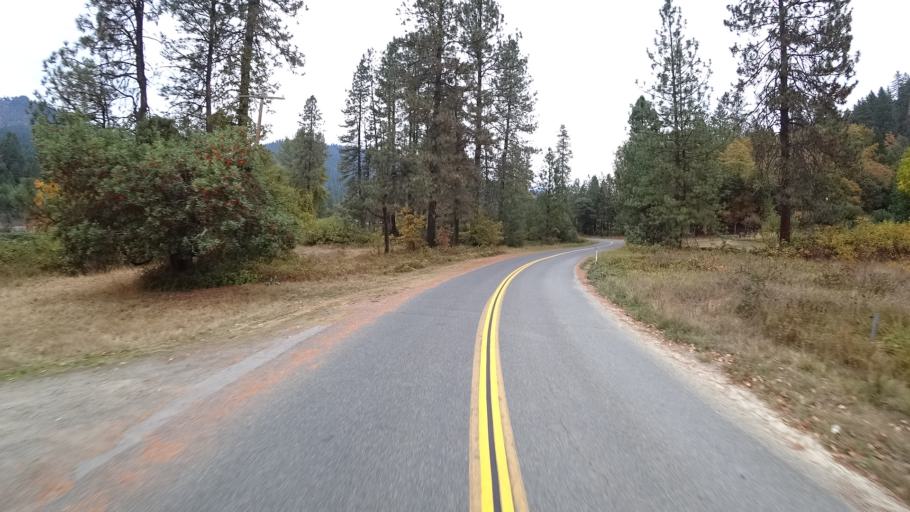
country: US
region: California
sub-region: Siskiyou County
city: Happy Camp
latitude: 41.7815
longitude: -123.3926
